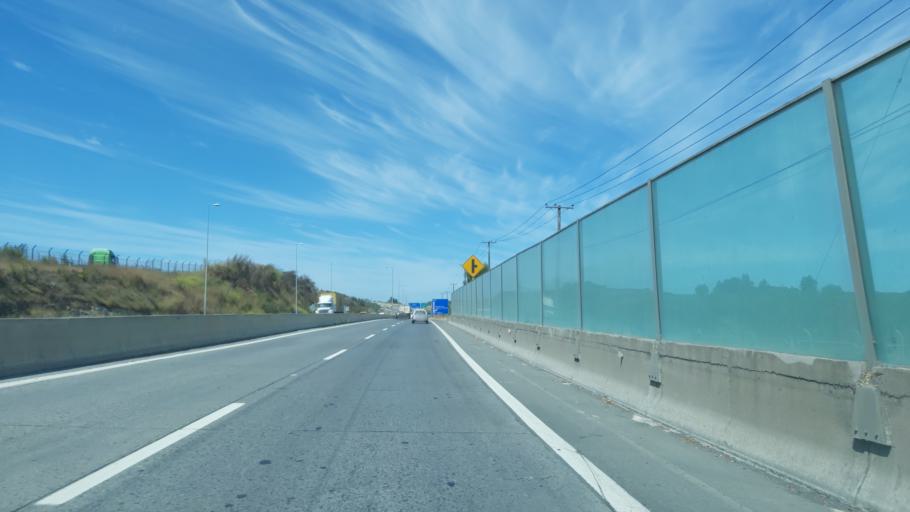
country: CL
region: Biobio
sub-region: Provincia de Concepcion
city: Coronel
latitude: -37.0406
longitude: -73.1362
